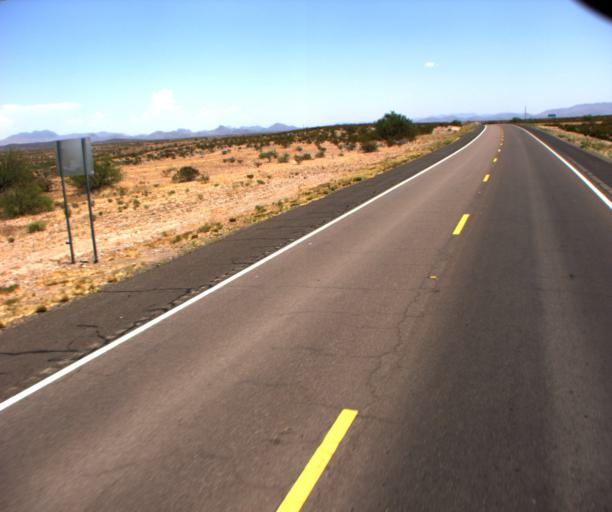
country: US
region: Arizona
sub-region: Graham County
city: Safford
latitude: 32.8062
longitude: -109.5818
